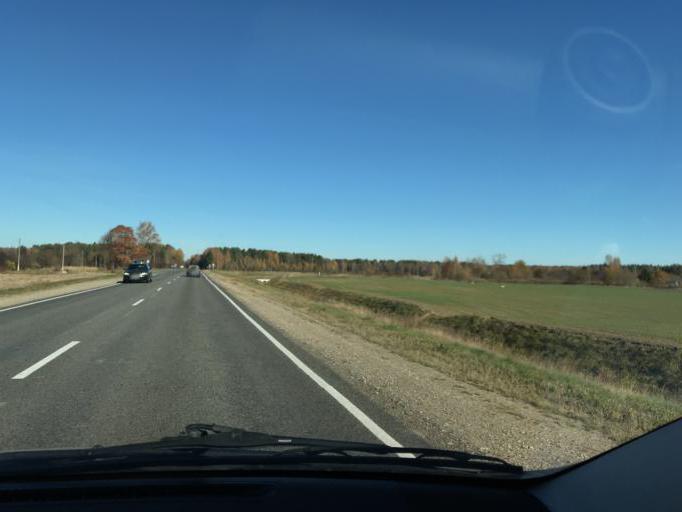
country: BY
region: Vitebsk
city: Lyepyel'
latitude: 55.0547
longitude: 28.7516
